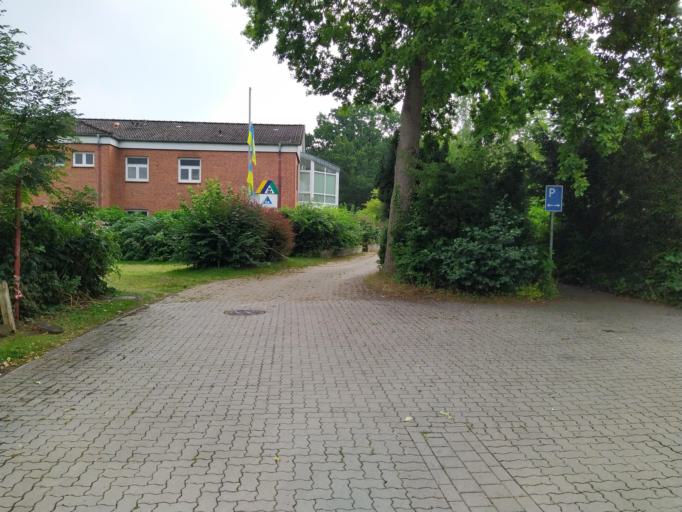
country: DE
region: Lower Saxony
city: Wingst
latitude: 53.7434
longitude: 9.0871
